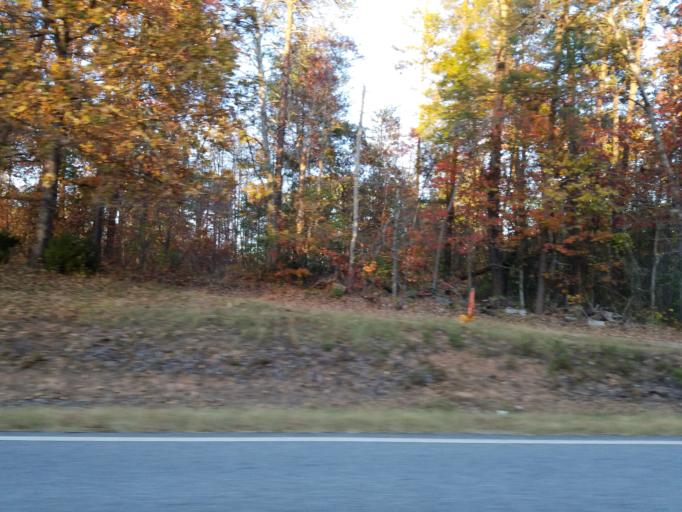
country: US
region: Georgia
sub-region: Lumpkin County
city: Dahlonega
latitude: 34.5235
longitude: -84.0500
